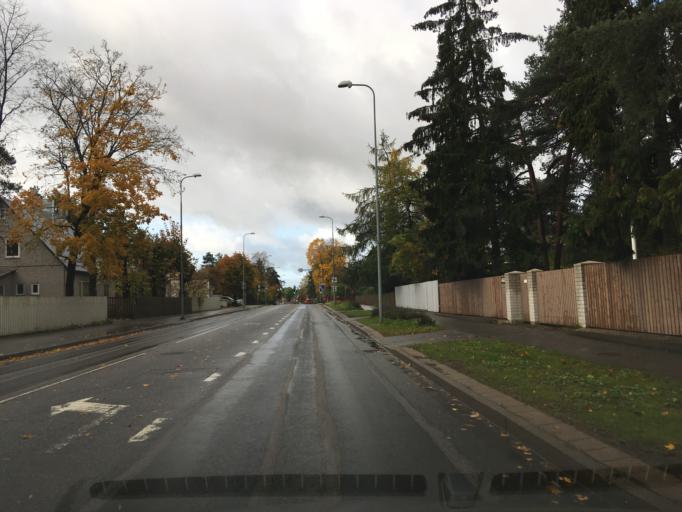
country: EE
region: Harju
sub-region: Saue vald
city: Laagri
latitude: 59.3722
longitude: 24.6424
